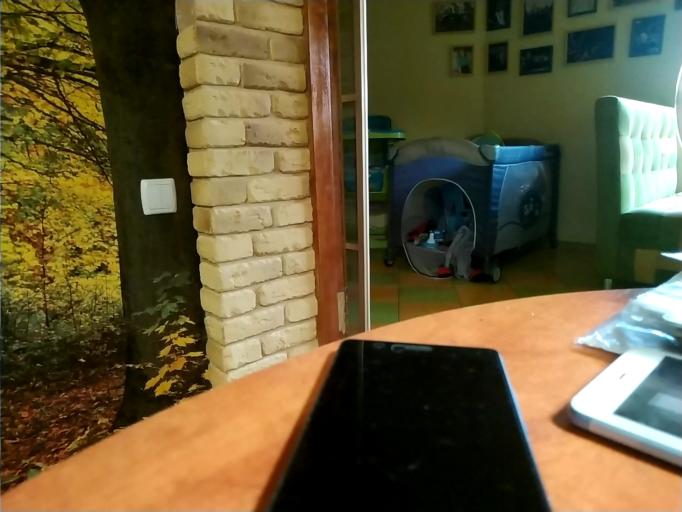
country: RU
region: Kaluga
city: Khvastovichi
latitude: 53.6898
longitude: 35.4352
